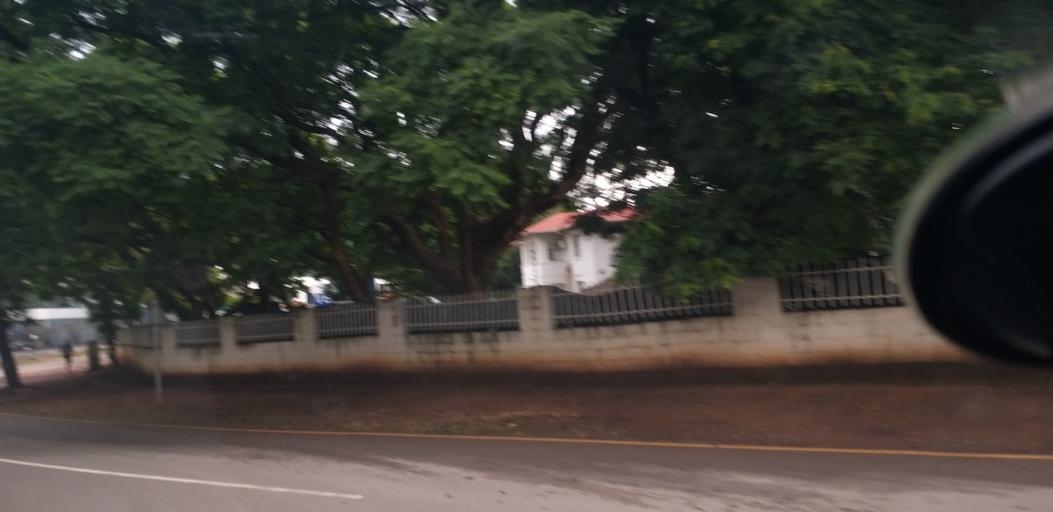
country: ZM
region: Lusaka
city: Lusaka
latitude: -15.4148
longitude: 28.3012
